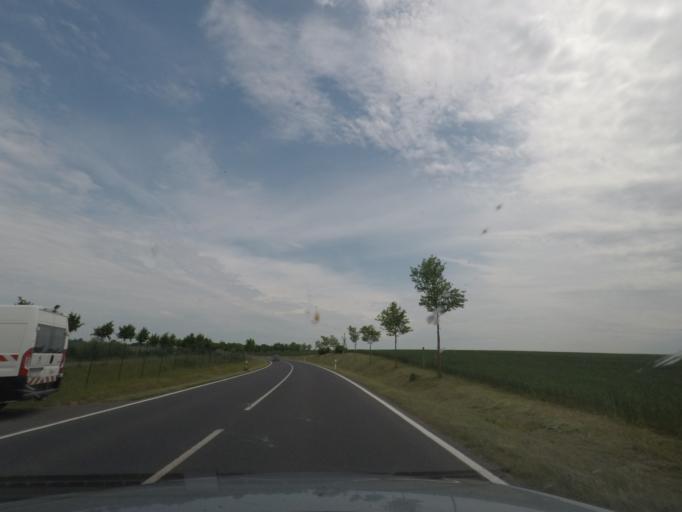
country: DE
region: Brandenburg
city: Grunow
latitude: 53.3387
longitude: 13.9372
